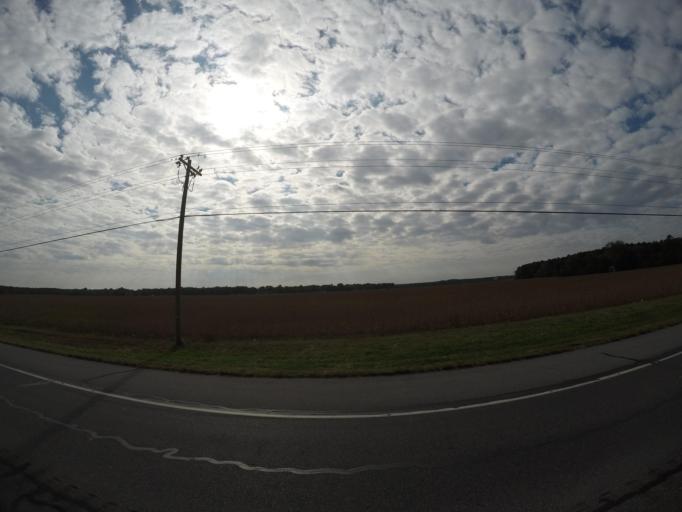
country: US
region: Delaware
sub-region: Sussex County
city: Bridgeville
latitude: 38.7090
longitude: -75.5406
